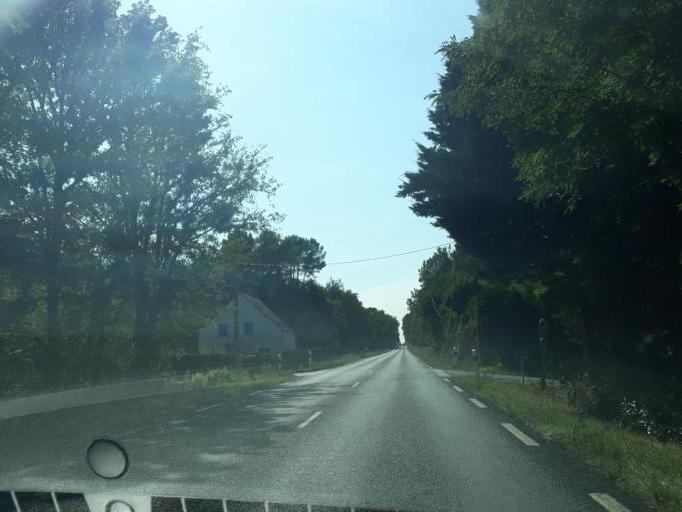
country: FR
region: Centre
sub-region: Departement du Loir-et-Cher
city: Chatillon-sur-Cher
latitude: 47.2869
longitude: 1.5156
